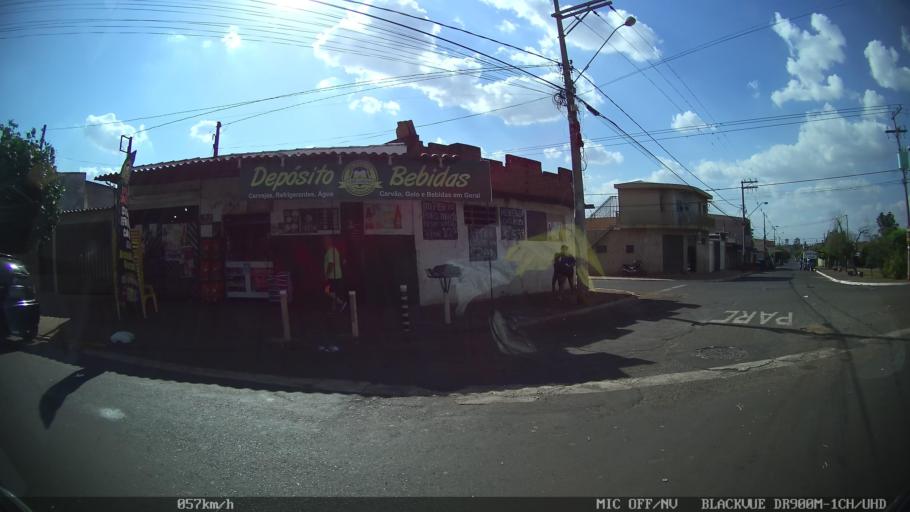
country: BR
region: Sao Paulo
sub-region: Ribeirao Preto
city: Ribeirao Preto
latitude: -21.2029
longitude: -47.8501
